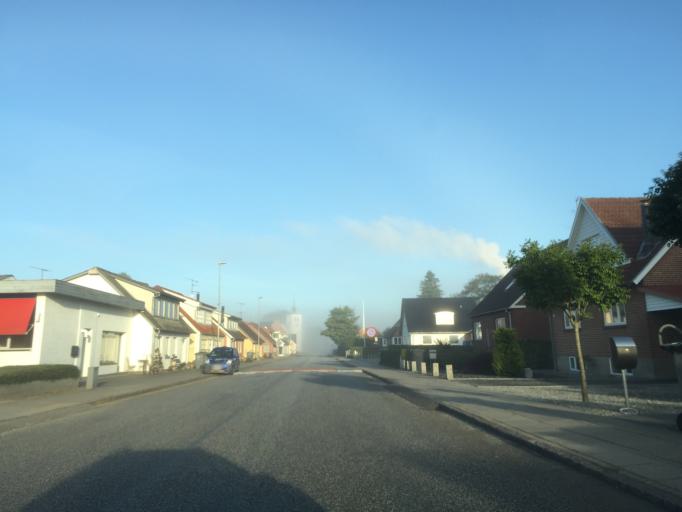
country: DK
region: Central Jutland
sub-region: Viborg Kommune
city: Bjerringbro
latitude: 56.3067
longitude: 9.5975
